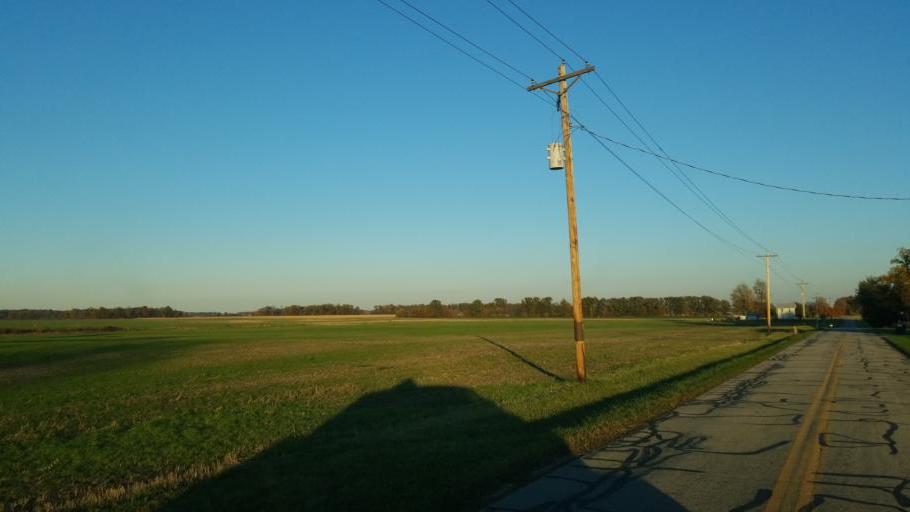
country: US
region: Ohio
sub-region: Sandusky County
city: Mount Carmel
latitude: 41.2125
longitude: -82.9641
